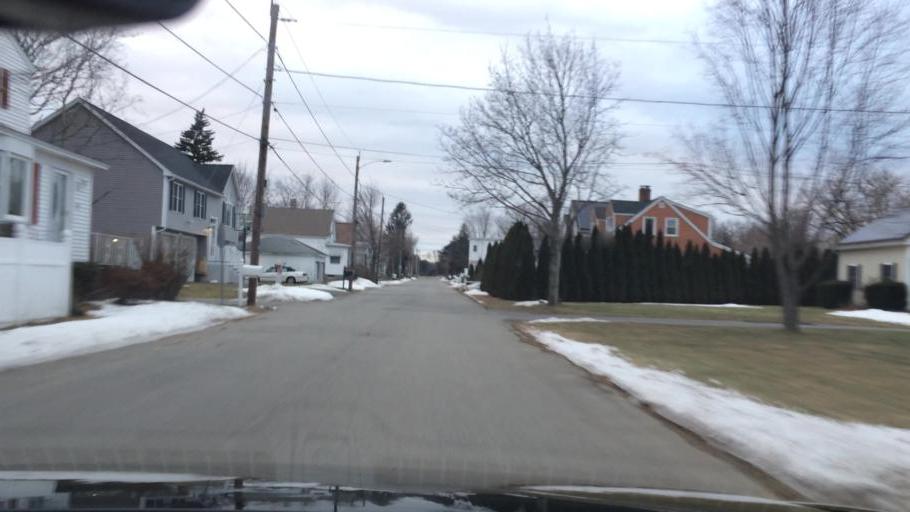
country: US
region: Massachusetts
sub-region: Essex County
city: North Andover
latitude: 42.7375
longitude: -71.1286
